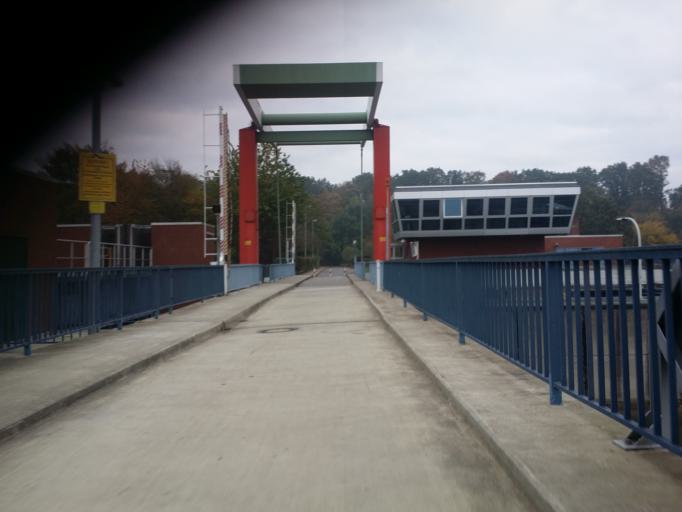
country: DE
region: Lower Saxony
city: Lemwerder
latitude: 53.1602
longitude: 8.6470
